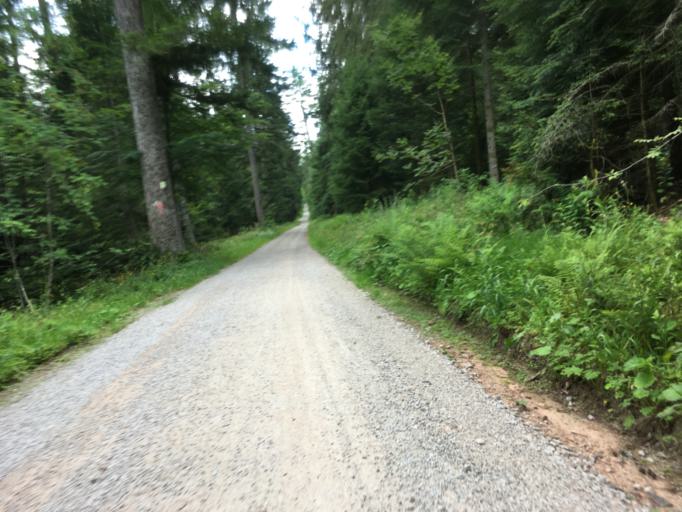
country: DE
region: Baden-Wuerttemberg
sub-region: Karlsruhe Region
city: Freudenstadt
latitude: 48.4484
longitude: 8.4090
